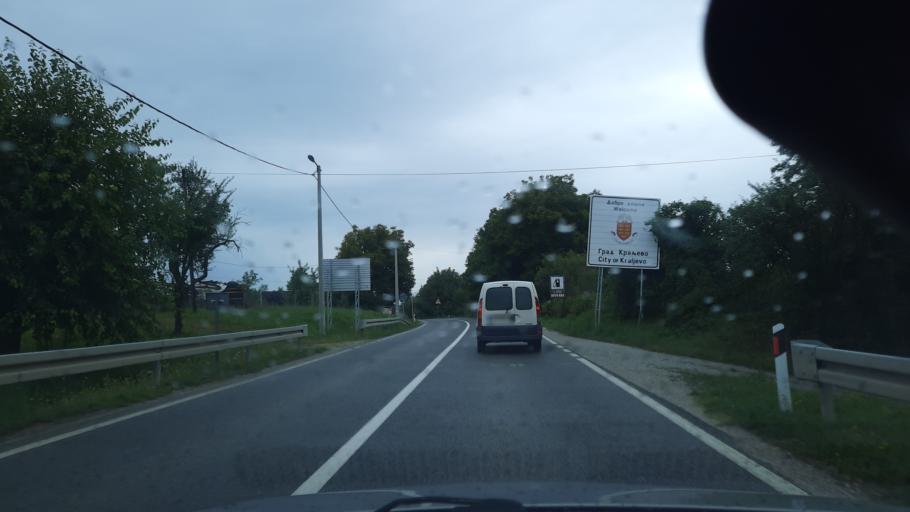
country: RS
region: Central Serbia
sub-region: Raski Okrug
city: Kraljevo
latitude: 43.8074
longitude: 20.7854
